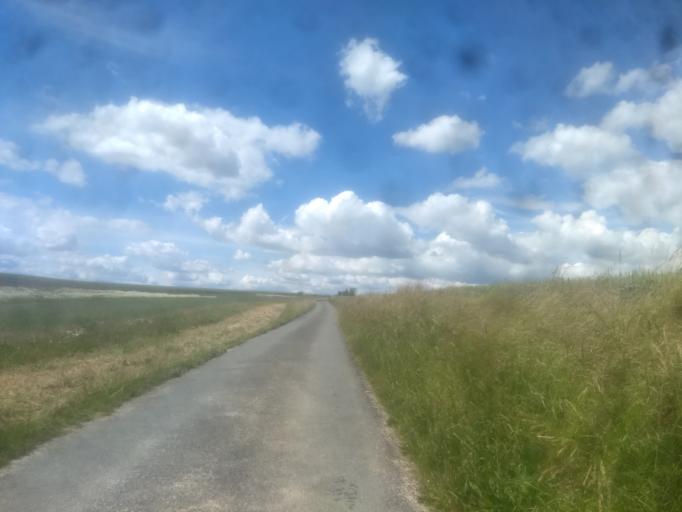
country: FR
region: Nord-Pas-de-Calais
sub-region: Departement du Pas-de-Calais
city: Tilloy-les-Mofflaines
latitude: 50.2334
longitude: 2.8362
